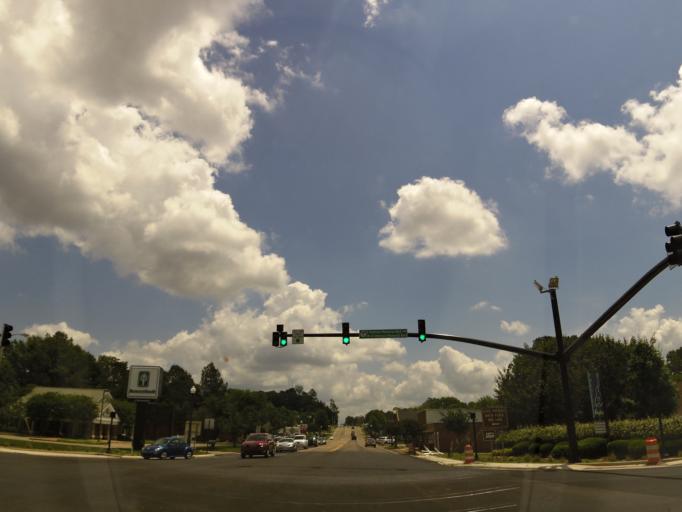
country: US
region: Mississippi
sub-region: Lee County
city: Tupelo
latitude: 34.2574
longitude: -88.6835
